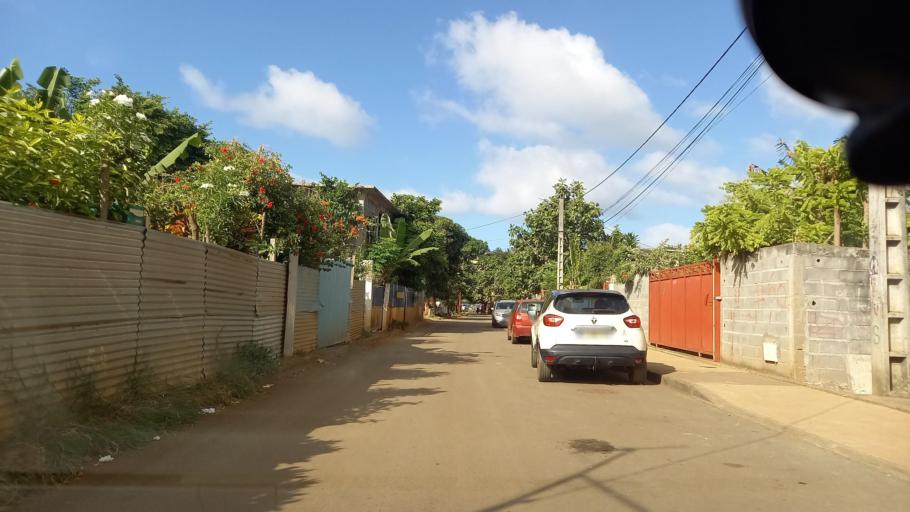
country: YT
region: Bandrele
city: Bandrele
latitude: -12.9124
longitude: 45.1937
